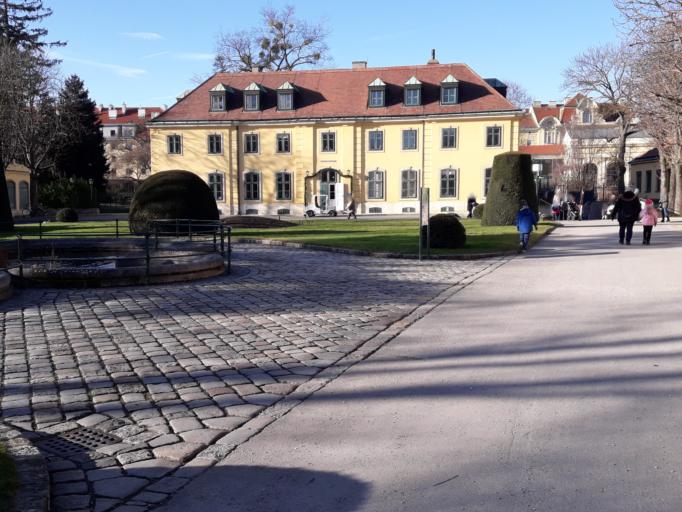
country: AT
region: Lower Austria
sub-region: Politischer Bezirk Modling
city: Vosendorf
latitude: 48.1826
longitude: 16.3019
